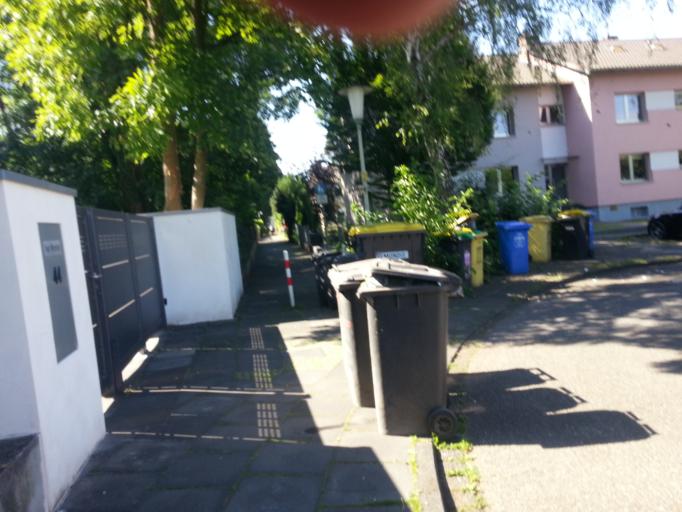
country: DE
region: North Rhine-Westphalia
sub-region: Regierungsbezirk Koln
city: Bonn
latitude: 50.7456
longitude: 7.1030
